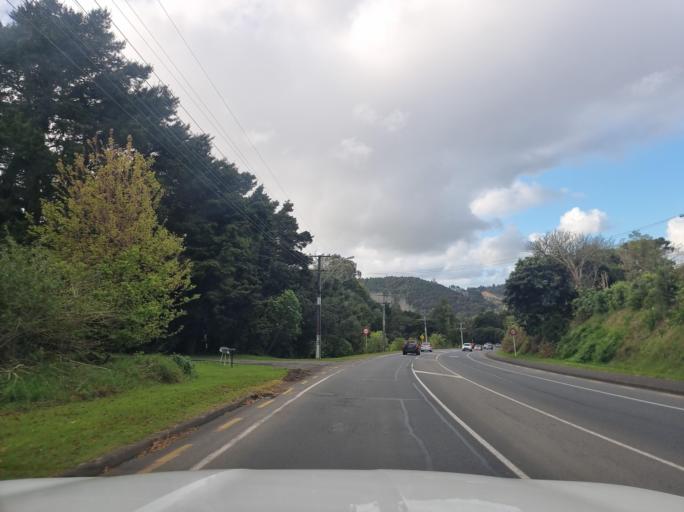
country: NZ
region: Northland
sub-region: Whangarei
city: Whangarei
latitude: -35.7386
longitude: 174.2831
